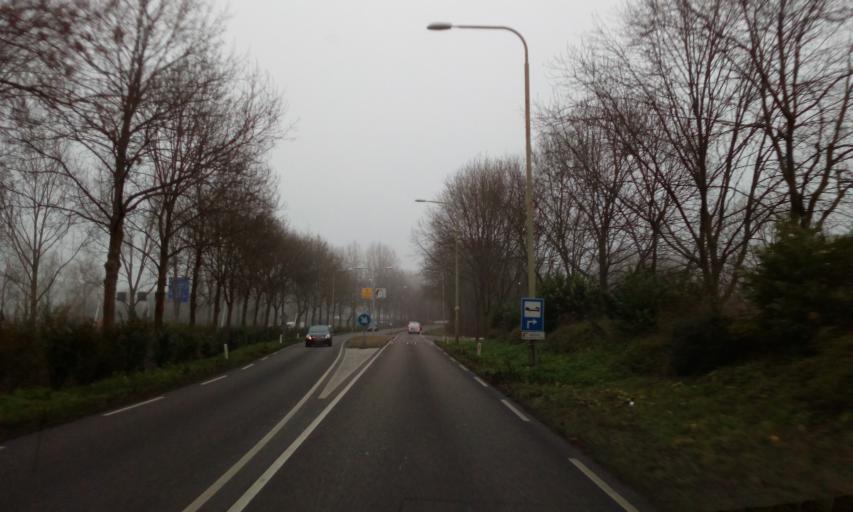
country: NL
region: South Holland
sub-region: Gemeente Capelle aan den IJssel
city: Capelle aan den IJssel
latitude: 51.9774
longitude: 4.6150
